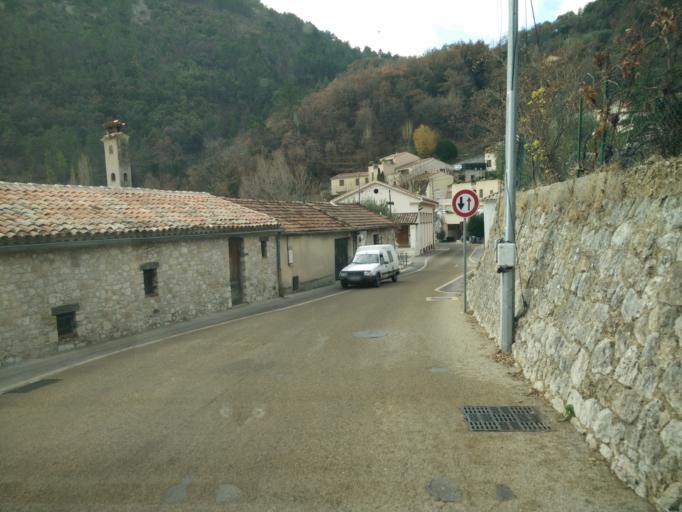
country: FR
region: Provence-Alpes-Cote d'Azur
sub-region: Departement des Alpes-Maritimes
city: Le Broc
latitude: 43.8076
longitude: 7.1671
